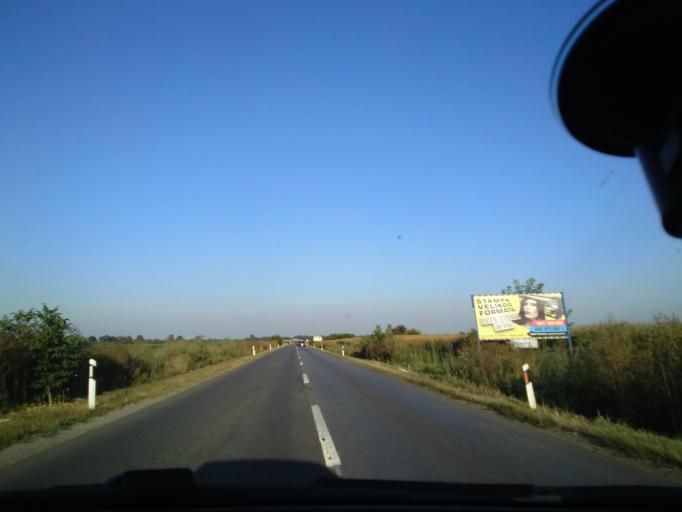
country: RS
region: Autonomna Pokrajina Vojvodina
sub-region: Juznobacki Okrug
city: Backi Petrovac
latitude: 45.3433
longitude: 19.6413
